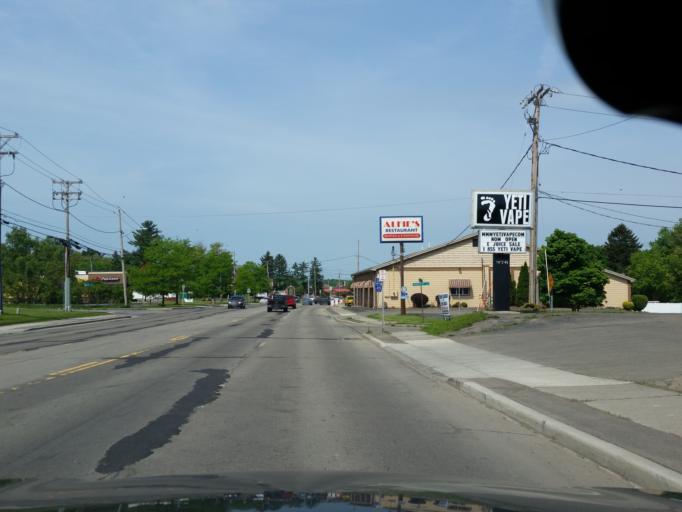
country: US
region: New York
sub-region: Chautauqua County
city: Jamestown West
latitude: 42.0976
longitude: -79.2923
